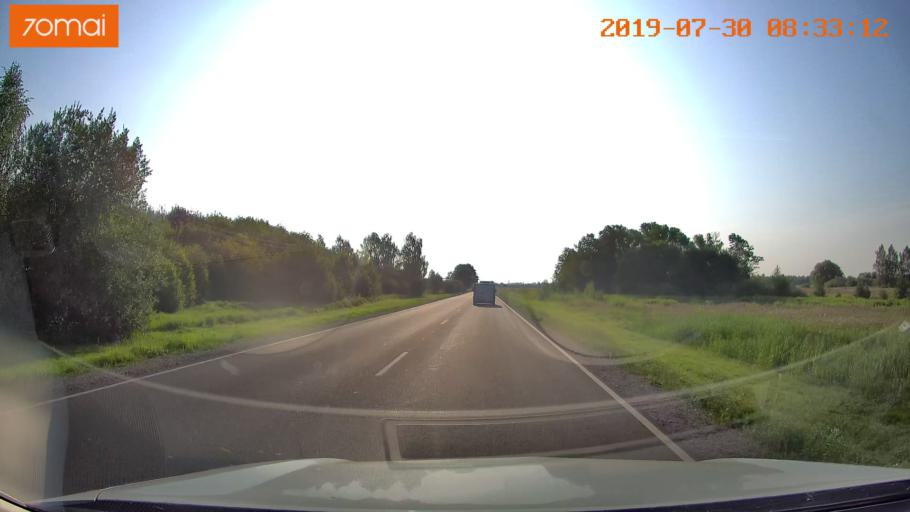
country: RU
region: Kaliningrad
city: Chernyakhovsk
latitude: 54.6363
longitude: 21.7419
